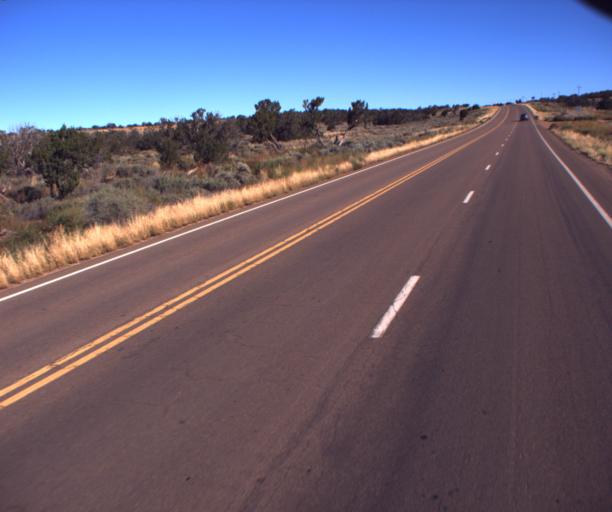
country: US
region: Arizona
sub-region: Navajo County
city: Snowflake
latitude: 34.5352
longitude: -110.0808
